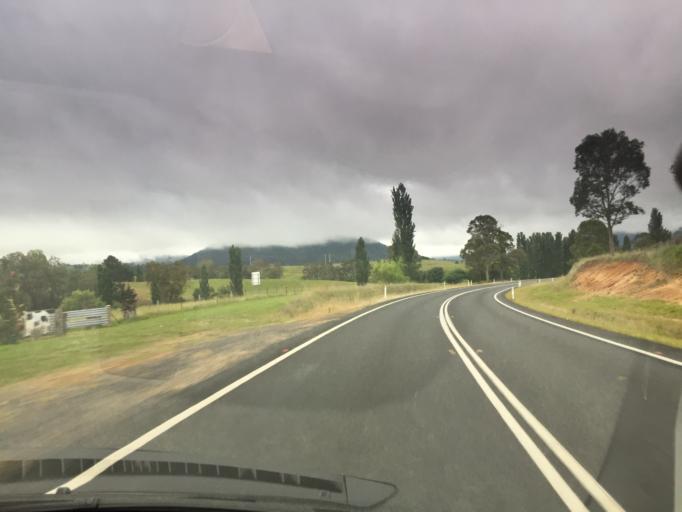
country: AU
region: New South Wales
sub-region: Bega Valley
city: Bega
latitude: -36.6130
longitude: 149.5235
